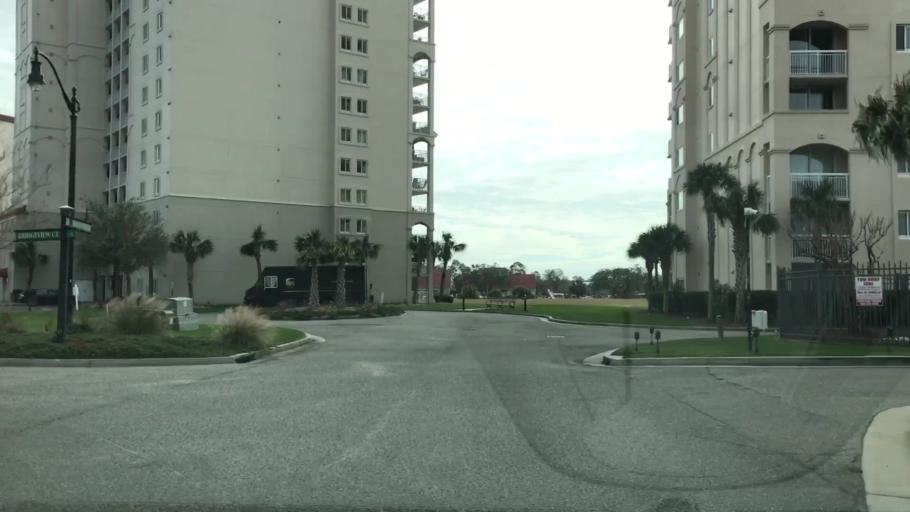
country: US
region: South Carolina
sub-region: Horry County
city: North Myrtle Beach
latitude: 33.8043
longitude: -78.7460
